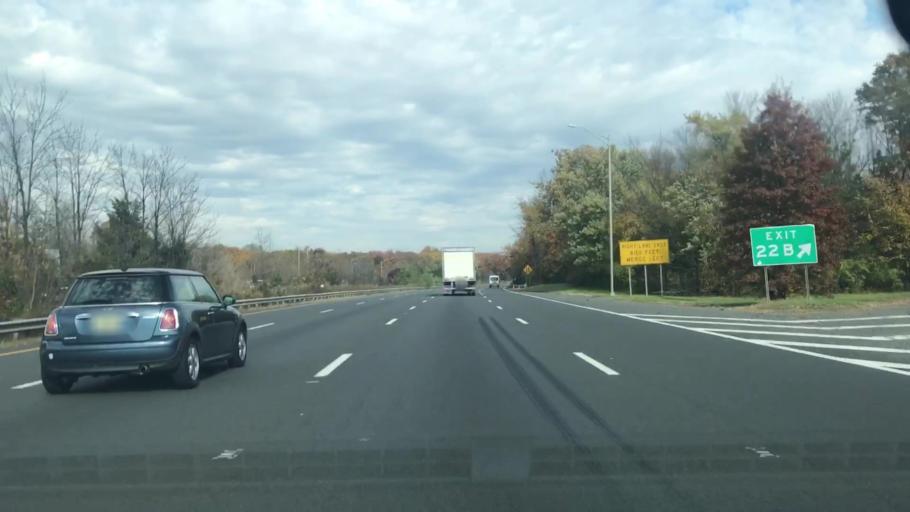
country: US
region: New Jersey
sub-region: Somerset County
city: Bedminster
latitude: 40.6585
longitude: -74.6440
